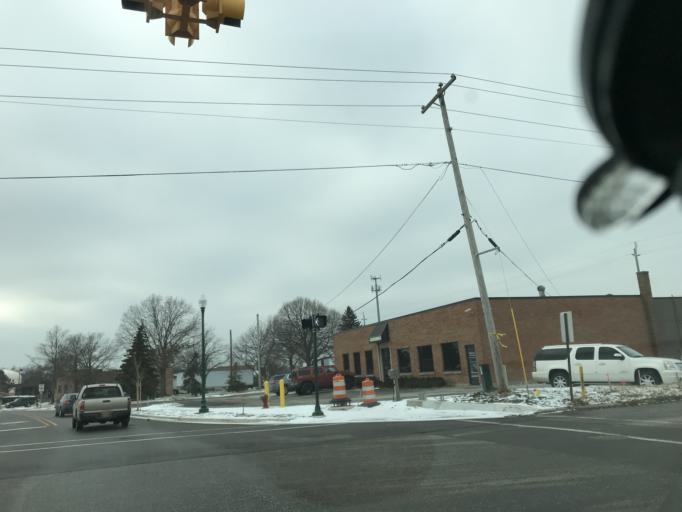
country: US
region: Michigan
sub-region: Ottawa County
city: Zeeland
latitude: 42.8139
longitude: -86.0287
